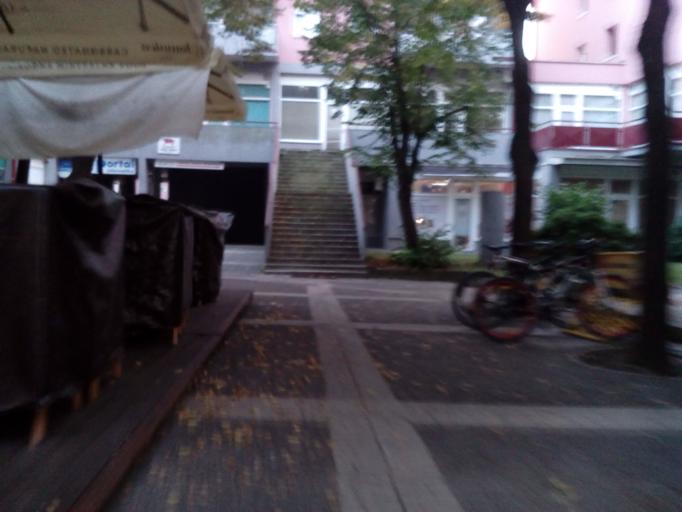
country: HR
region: Vukovarsko-Srijemska
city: Vinkovci
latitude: 45.2935
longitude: 18.8035
